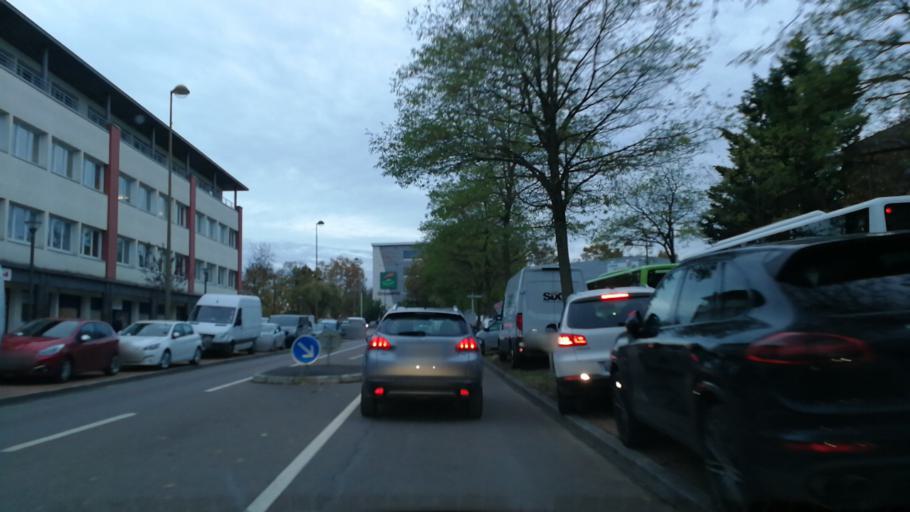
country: FR
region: Bourgogne
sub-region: Departement de la Cote-d'Or
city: Saint-Apollinaire
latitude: 47.3301
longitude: 5.0561
